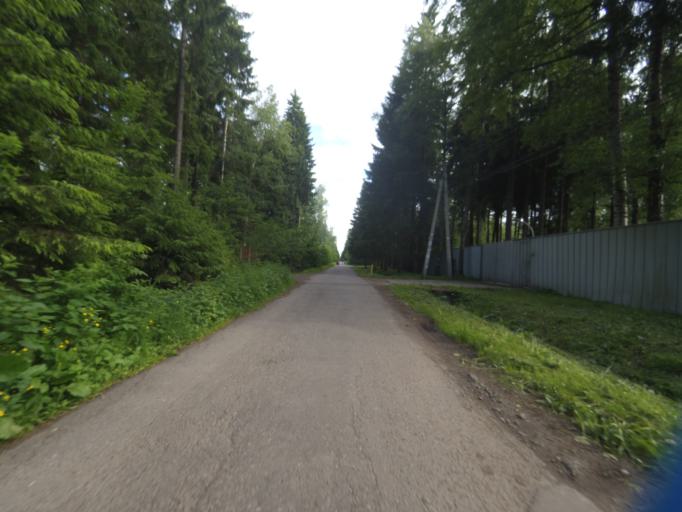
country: RU
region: Moskovskaya
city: Nekrasovskiy
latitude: 56.1185
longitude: 37.5173
